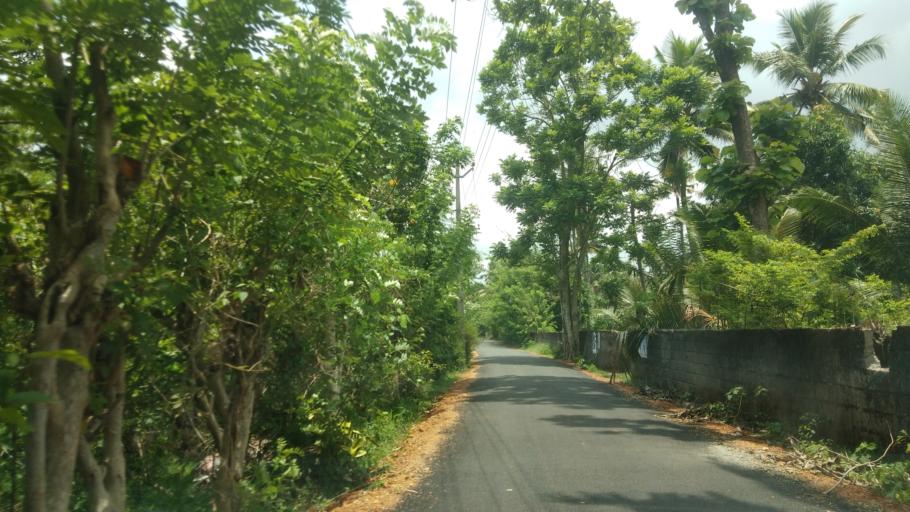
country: IN
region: Kerala
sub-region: Alappuzha
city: Shertallai
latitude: 9.6531
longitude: 76.3310
